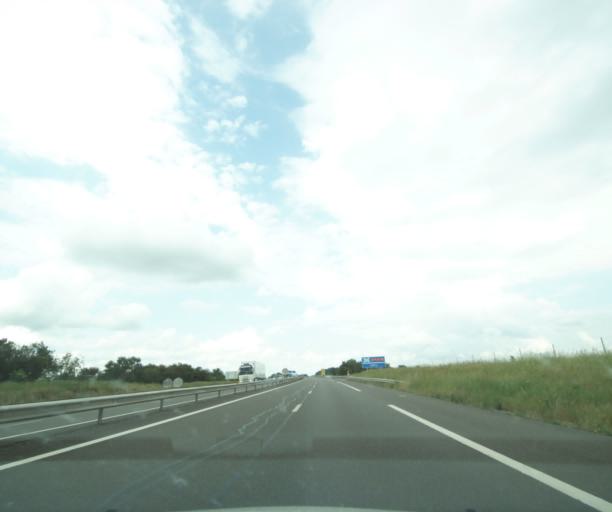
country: FR
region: Auvergne
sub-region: Departement de l'Allier
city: Ebreuil
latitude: 46.0863
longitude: 3.1315
